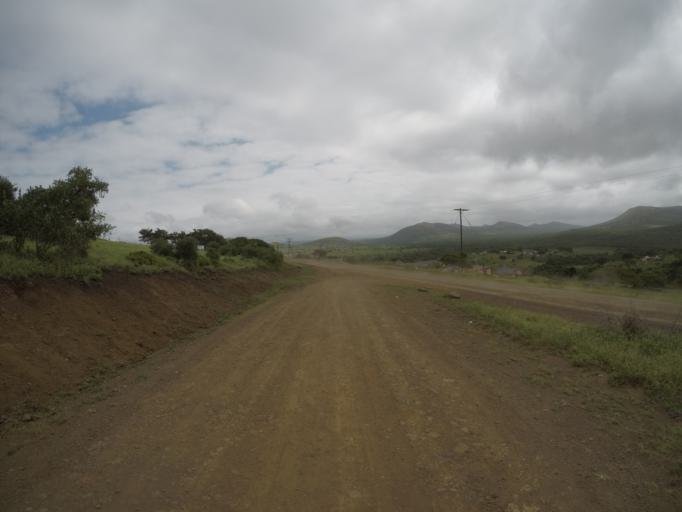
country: ZA
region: KwaZulu-Natal
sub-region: uThungulu District Municipality
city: Empangeni
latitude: -28.6260
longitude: 31.8701
